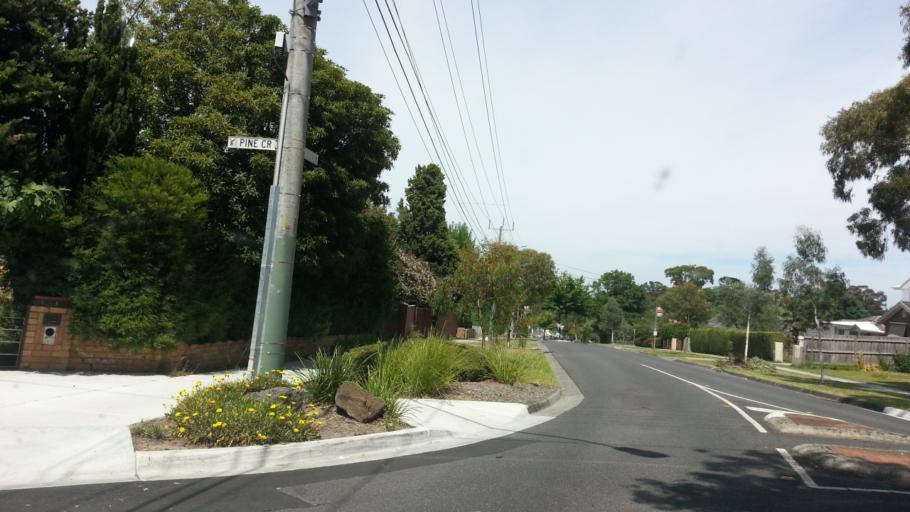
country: AU
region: Victoria
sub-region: Knox
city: Boronia
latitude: -37.8657
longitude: 145.2808
